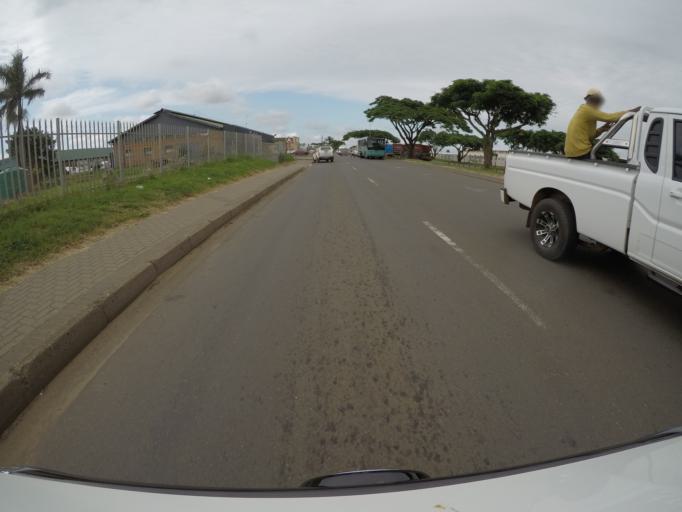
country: ZA
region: KwaZulu-Natal
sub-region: uThungulu District Municipality
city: Empangeni
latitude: -28.7767
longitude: 31.9004
